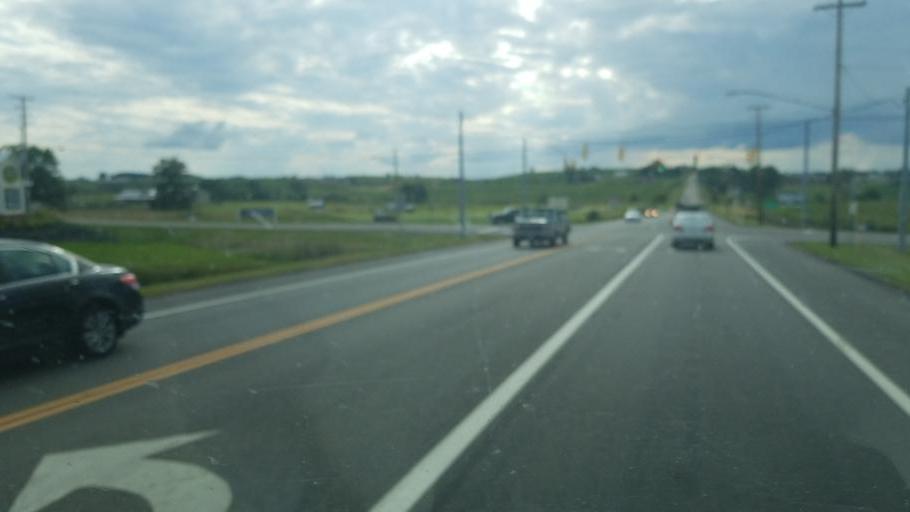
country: US
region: Ohio
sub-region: Tuscarawas County
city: Sugarcreek
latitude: 40.5099
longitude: -81.6091
